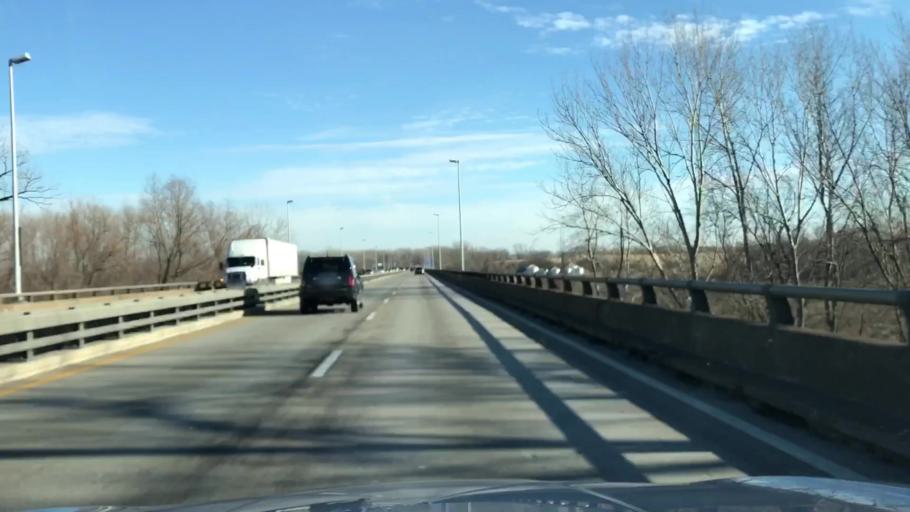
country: US
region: Missouri
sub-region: Saint Louis County
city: Glasgow Village
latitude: 38.7632
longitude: -90.1677
